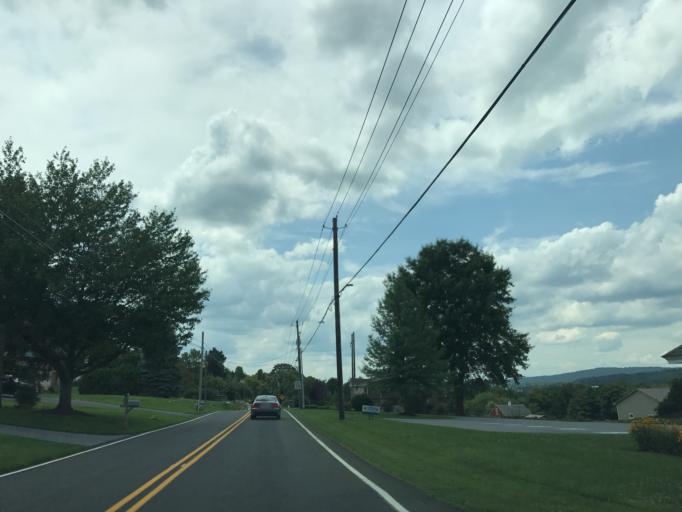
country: US
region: Pennsylvania
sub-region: Lancaster County
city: Penryn
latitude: 40.2077
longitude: -76.3802
